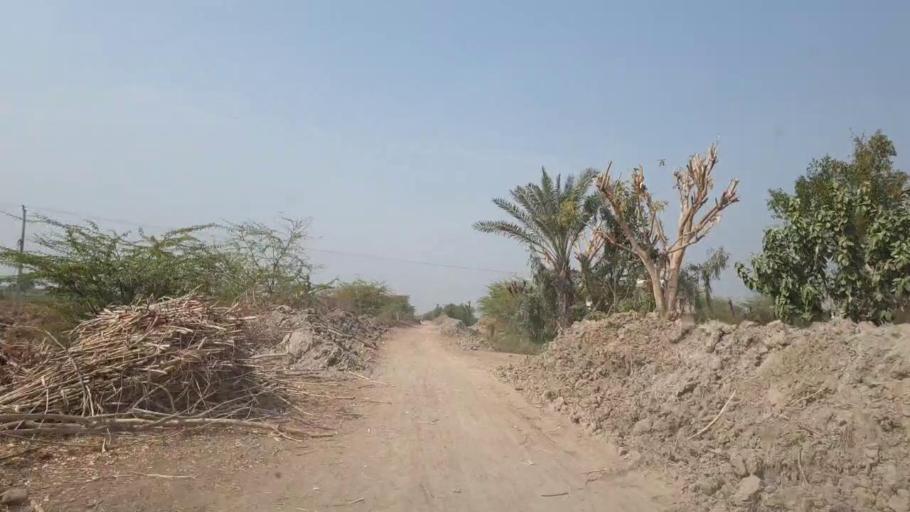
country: PK
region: Sindh
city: Mirpur Khas
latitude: 25.5676
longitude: 69.1427
